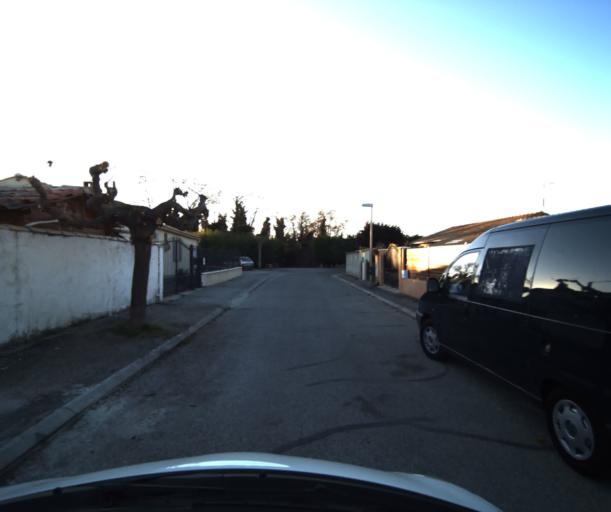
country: FR
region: Provence-Alpes-Cote d'Azur
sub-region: Departement du Vaucluse
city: Pertuis
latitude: 43.6887
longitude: 5.4933
